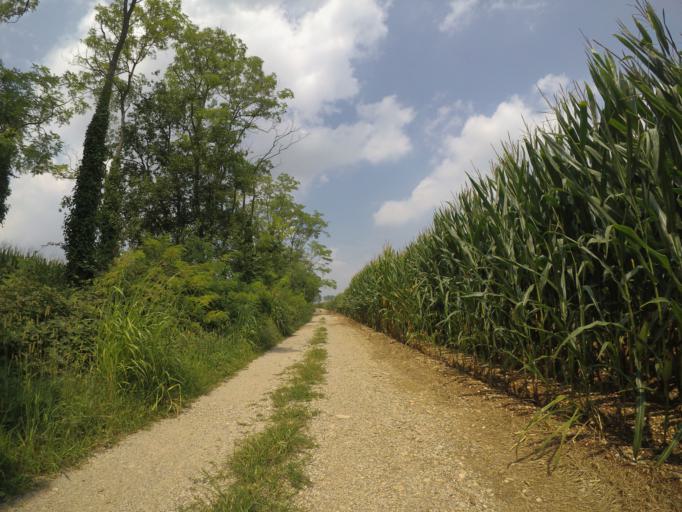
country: IT
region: Friuli Venezia Giulia
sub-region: Provincia di Udine
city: Codroipo
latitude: 45.9784
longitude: 13.0035
